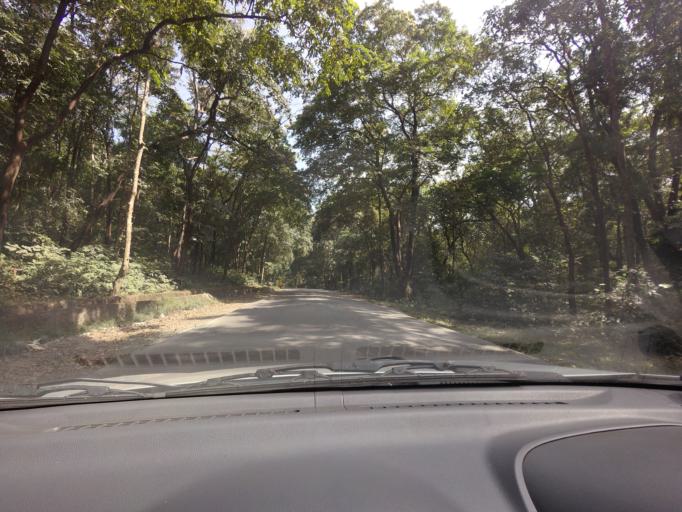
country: IN
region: Karnataka
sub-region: Hassan
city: Sakleshpur
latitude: 12.8279
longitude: 75.5742
